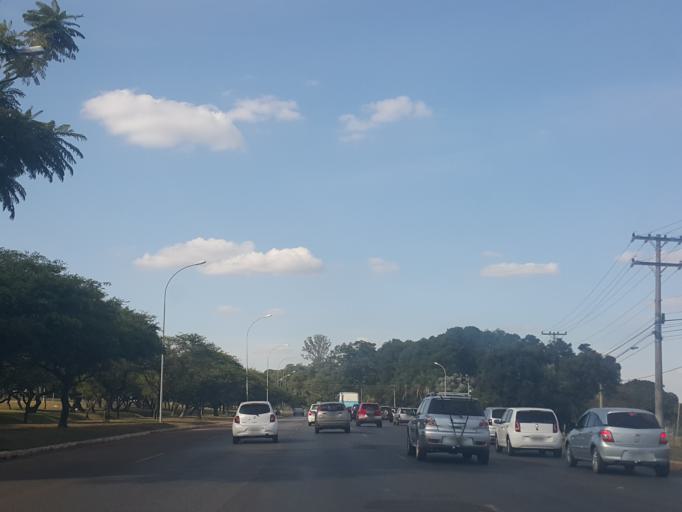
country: BR
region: Federal District
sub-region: Brasilia
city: Brasilia
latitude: -15.8078
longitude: -47.9306
